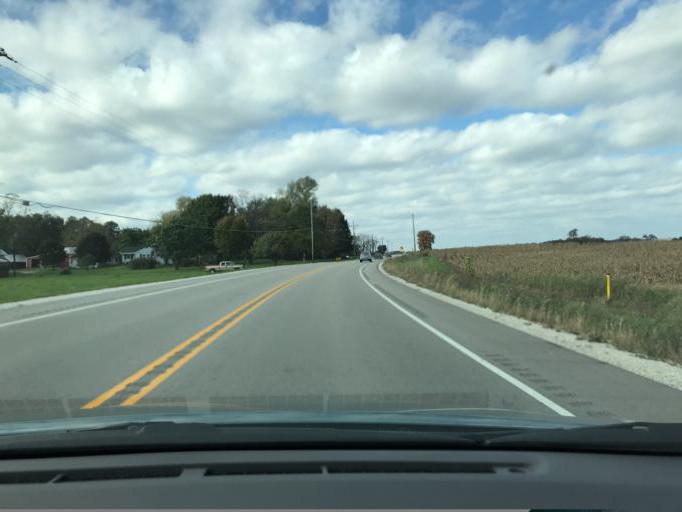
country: US
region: Wisconsin
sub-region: Racine County
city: Browns Lake
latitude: 42.6580
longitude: -88.2334
